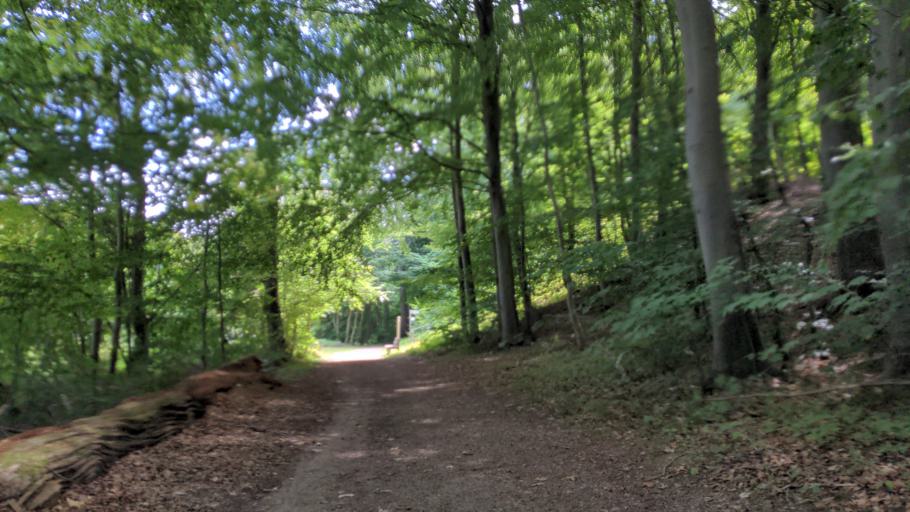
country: DE
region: Schleswig-Holstein
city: Eutin
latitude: 54.1834
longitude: 10.6287
